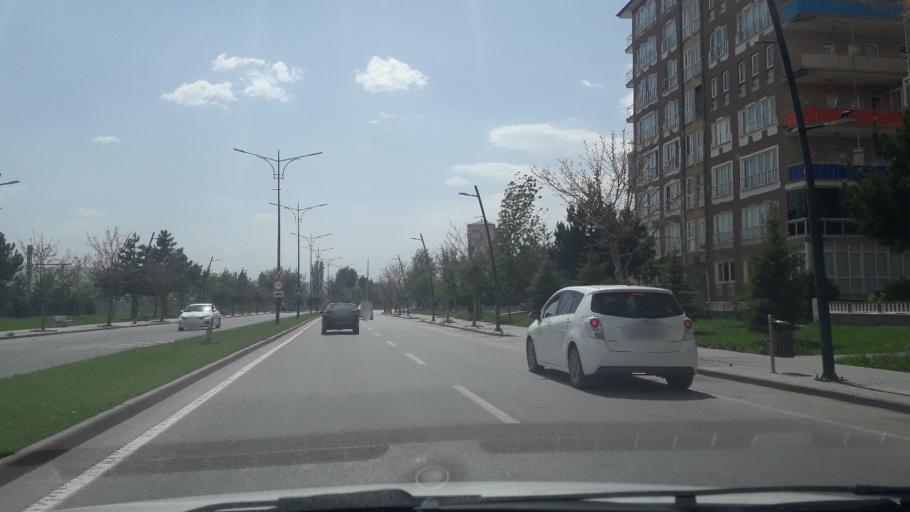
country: TR
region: Sivas
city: Sivas
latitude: 39.7276
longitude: 36.9754
